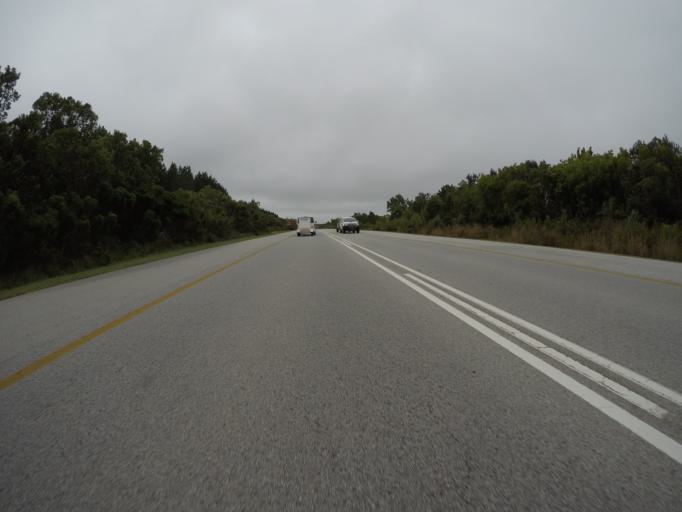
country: ZA
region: Eastern Cape
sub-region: Cacadu District Municipality
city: Kareedouw
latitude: -33.9661
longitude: 23.8792
